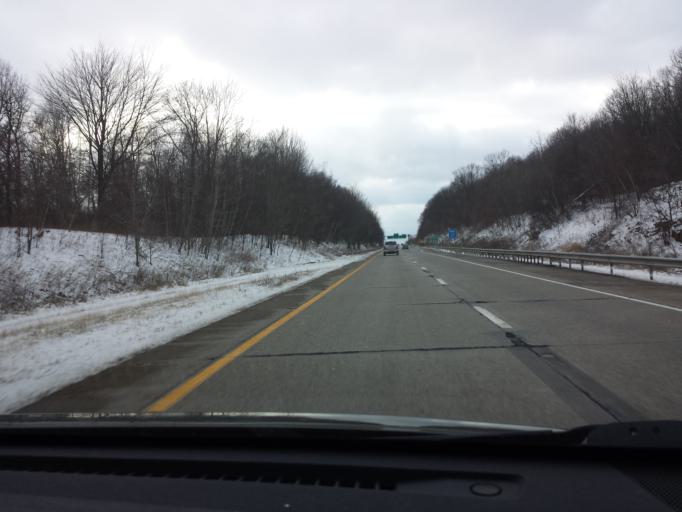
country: US
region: Pennsylvania
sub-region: Luzerne County
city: Harleigh
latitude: 41.0505
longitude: -75.9992
